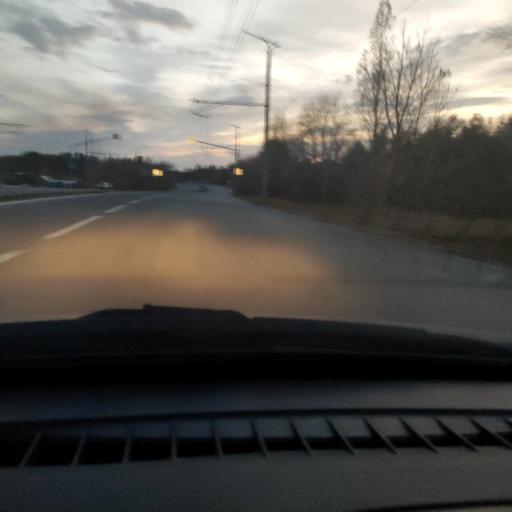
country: RU
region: Samara
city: Zhigulevsk
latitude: 53.5346
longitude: 49.5597
